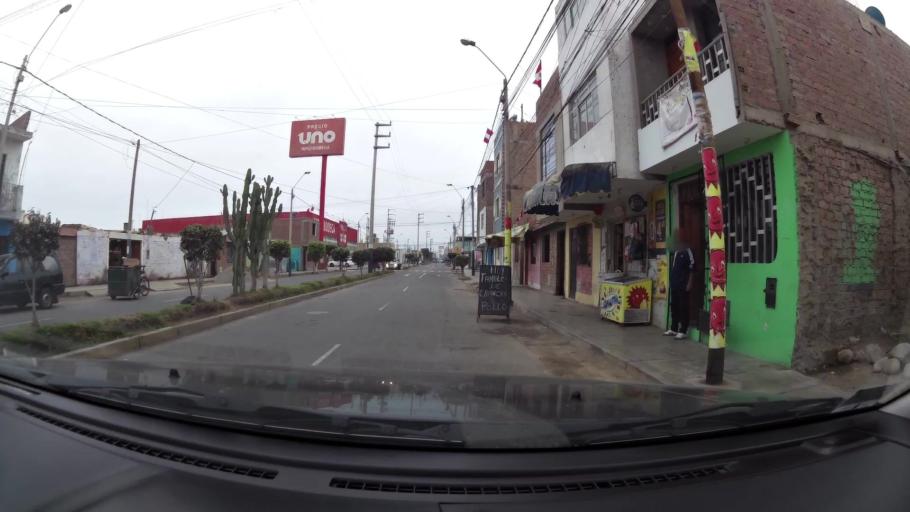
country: PE
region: Ica
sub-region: Provincia de Pisco
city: Pisco
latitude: -13.7169
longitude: -76.2040
